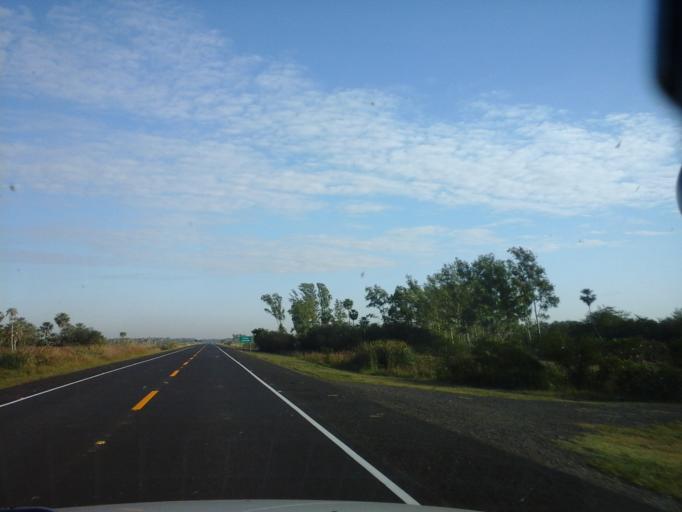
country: PY
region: Neembucu
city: Cerrito
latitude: -26.8812
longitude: -57.7412
